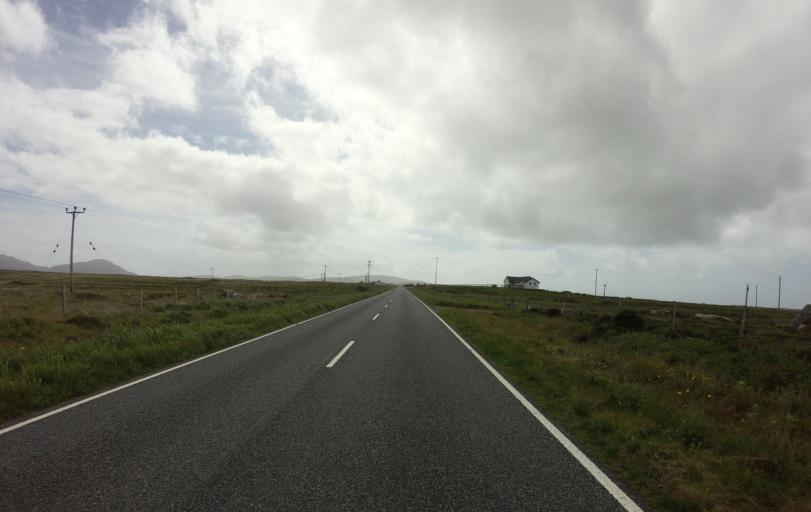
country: GB
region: Scotland
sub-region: Eilean Siar
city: Isle of South Uist
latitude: 57.1786
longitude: -7.3791
